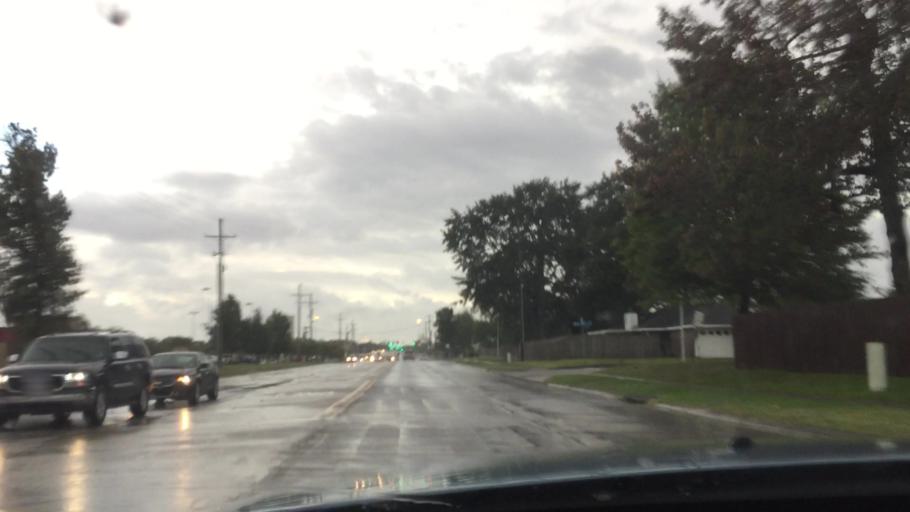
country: US
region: Louisiana
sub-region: East Baton Rouge Parish
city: Monticello
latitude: 30.4466
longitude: -91.0245
